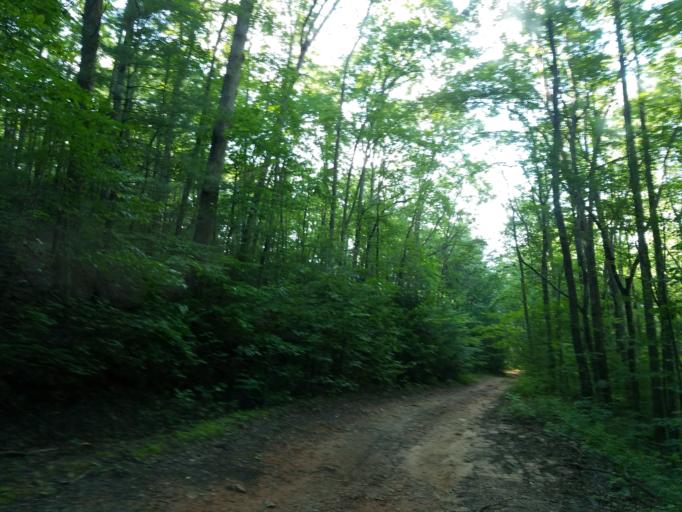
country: US
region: Georgia
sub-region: Dawson County
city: Dawsonville
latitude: 34.6227
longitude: -84.2354
